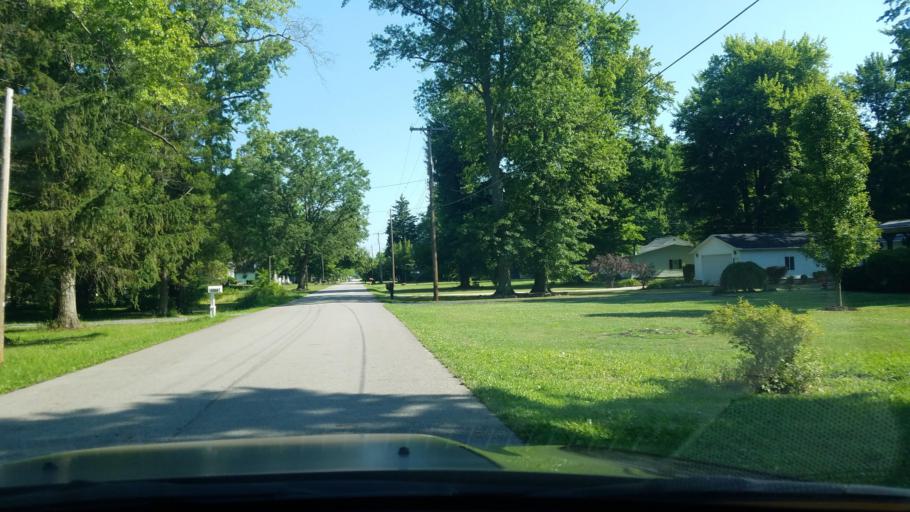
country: US
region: Ohio
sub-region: Trumbull County
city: Leavittsburg
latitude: 41.2644
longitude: -80.8880
